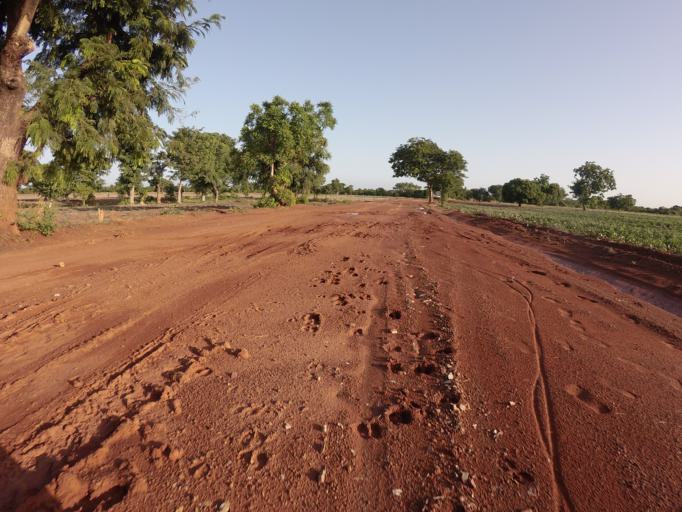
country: TG
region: Savanes
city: Sansanne-Mango
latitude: 10.3438
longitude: -0.0926
